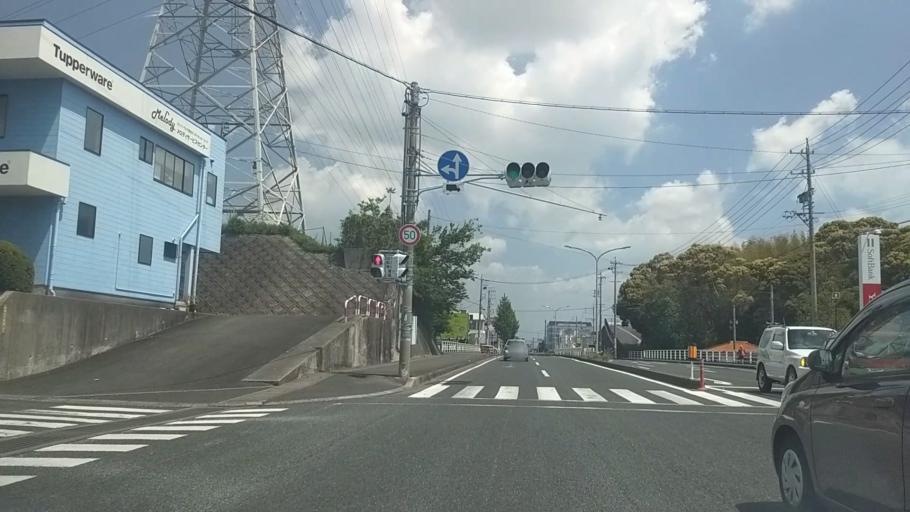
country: JP
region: Shizuoka
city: Hamamatsu
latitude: 34.7380
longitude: 137.7364
